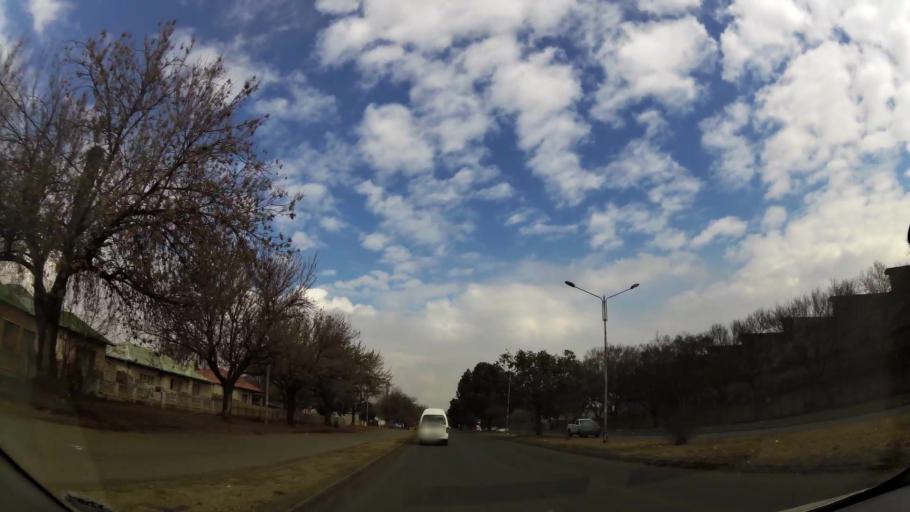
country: ZA
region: Gauteng
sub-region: Sedibeng District Municipality
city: Vereeniging
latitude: -26.6652
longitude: 27.9424
